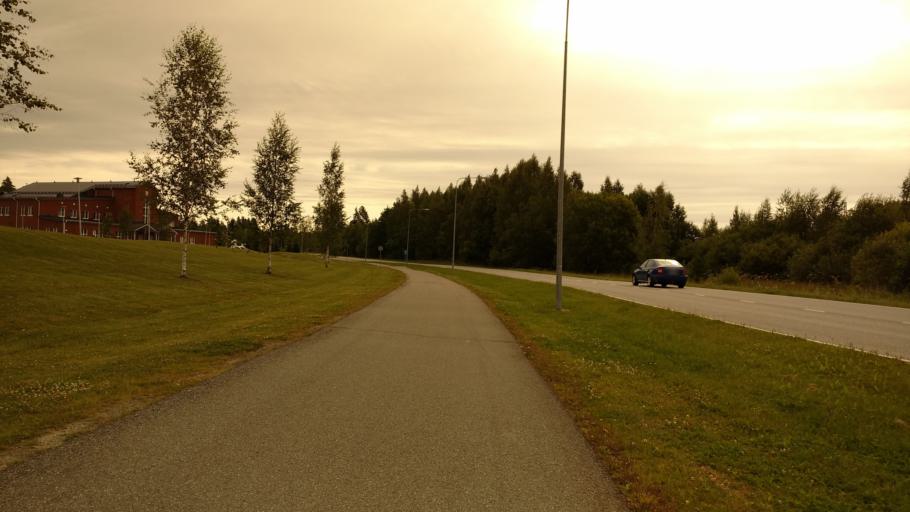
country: FI
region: Varsinais-Suomi
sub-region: Turku
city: Kaarina
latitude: 60.4454
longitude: 22.4096
